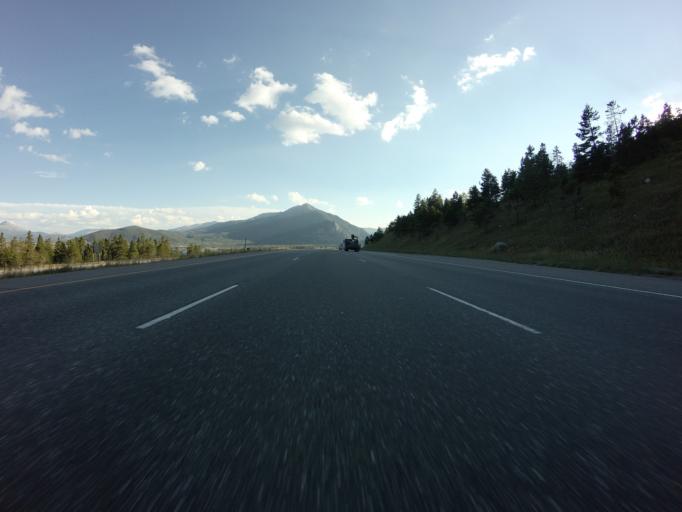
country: US
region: Colorado
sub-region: Summit County
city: Silverthorne
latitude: 39.6067
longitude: -106.0820
